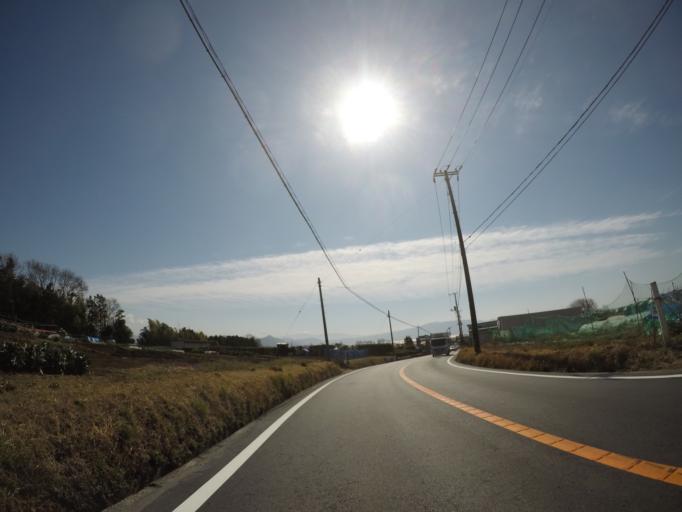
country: JP
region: Shizuoka
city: Numazu
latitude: 35.1338
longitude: 138.8362
